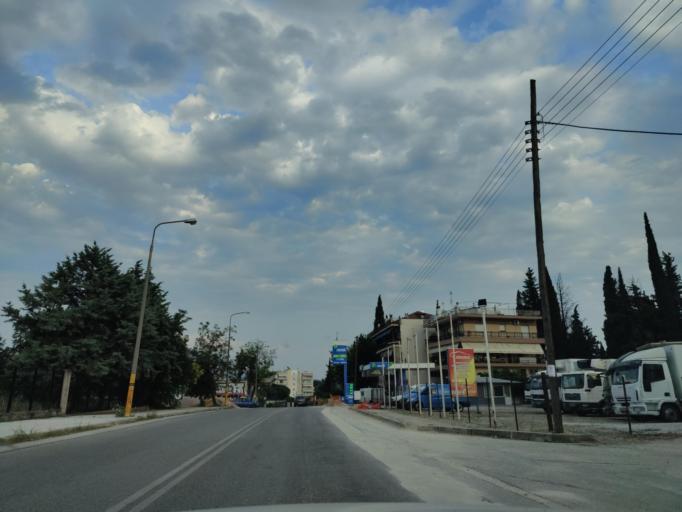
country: GR
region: East Macedonia and Thrace
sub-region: Nomos Dramas
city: Drama
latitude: 41.1510
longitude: 24.1343
